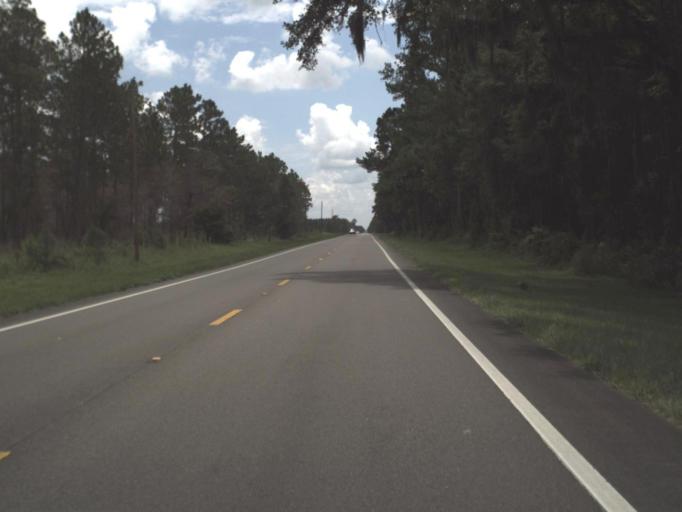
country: US
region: Florida
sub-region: Alachua County
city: Archer
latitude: 29.4806
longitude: -82.4882
